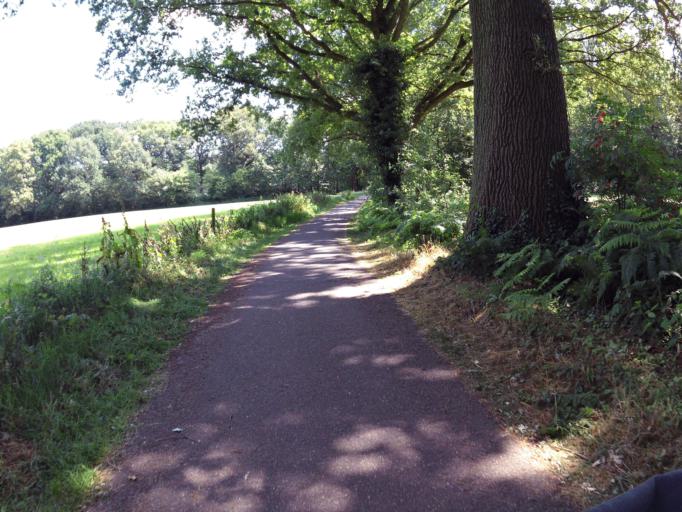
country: NL
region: North Brabant
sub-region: Gemeente Oisterwijk
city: Oisterwijk
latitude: 51.5613
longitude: 5.1869
